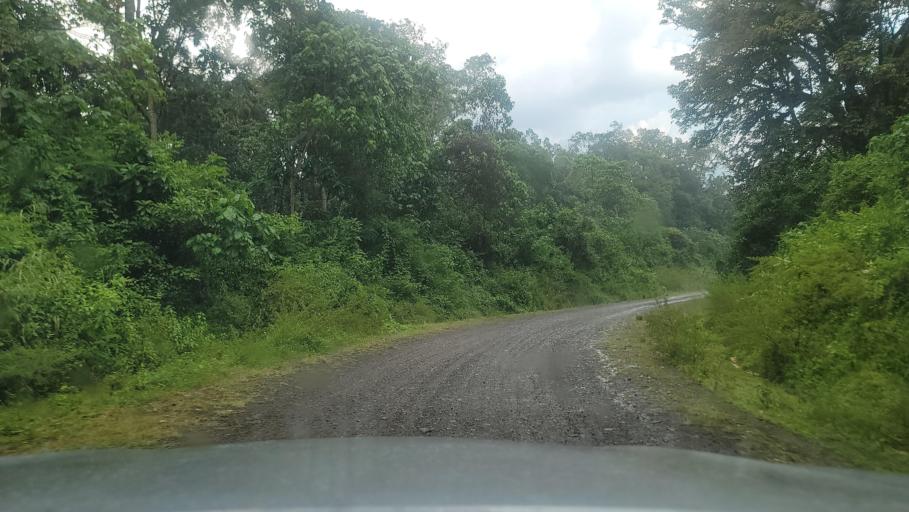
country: ET
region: Southern Nations, Nationalities, and People's Region
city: Bonga
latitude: 7.6635
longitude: 36.2453
